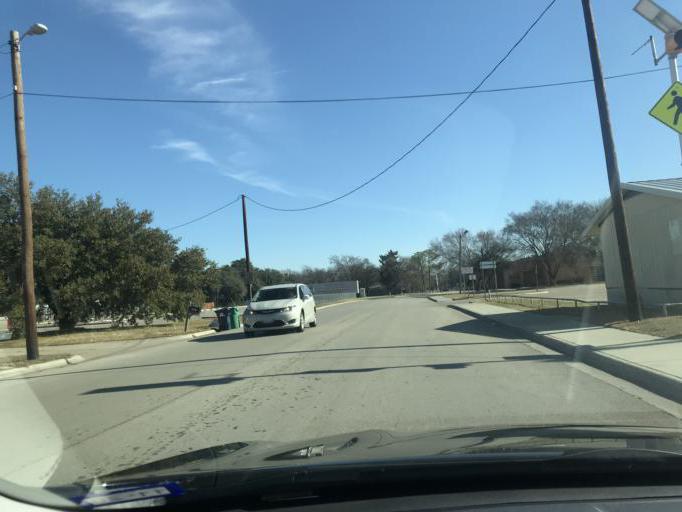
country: US
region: Texas
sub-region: Denton County
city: Denton
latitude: 33.2258
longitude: -97.1462
